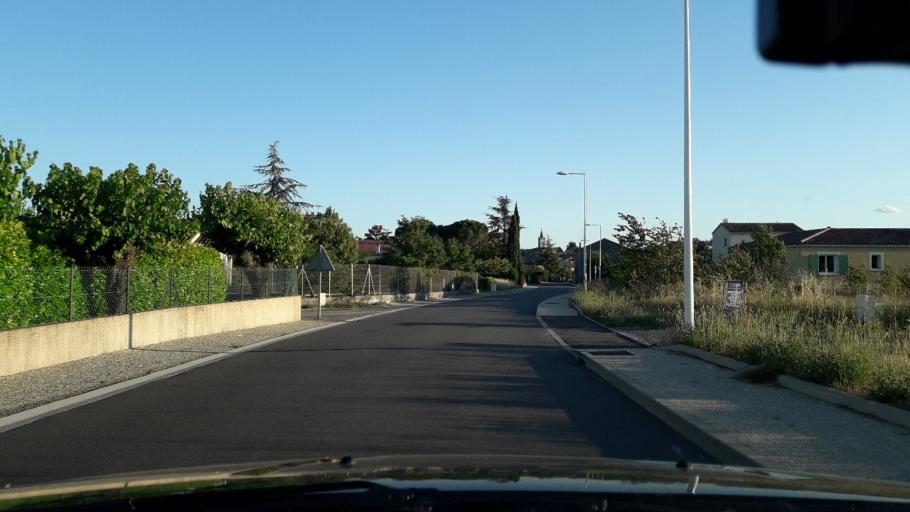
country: FR
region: Rhone-Alpes
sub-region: Departement de l'Ardeche
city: Lavilledieu
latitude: 44.5809
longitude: 4.4576
